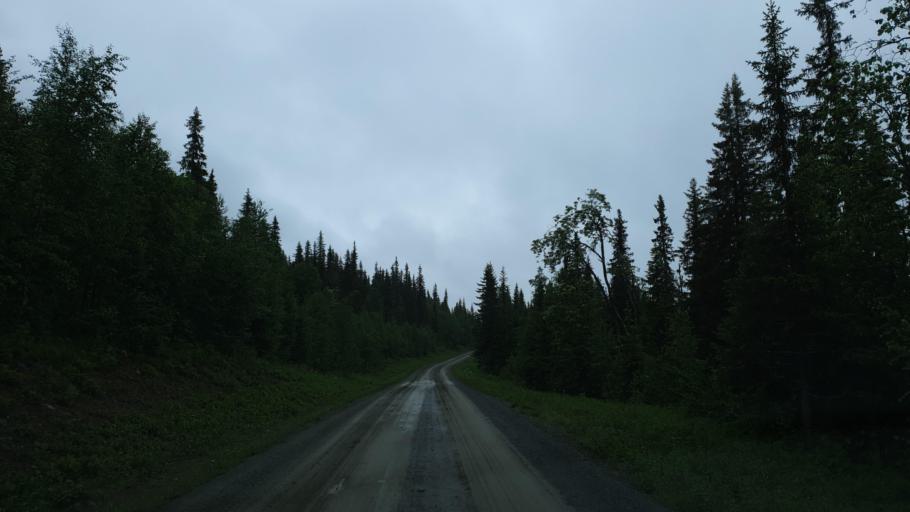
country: SE
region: Vaesterbotten
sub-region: Vilhelmina Kommun
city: Sjoberg
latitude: 65.3326
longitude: 15.9039
